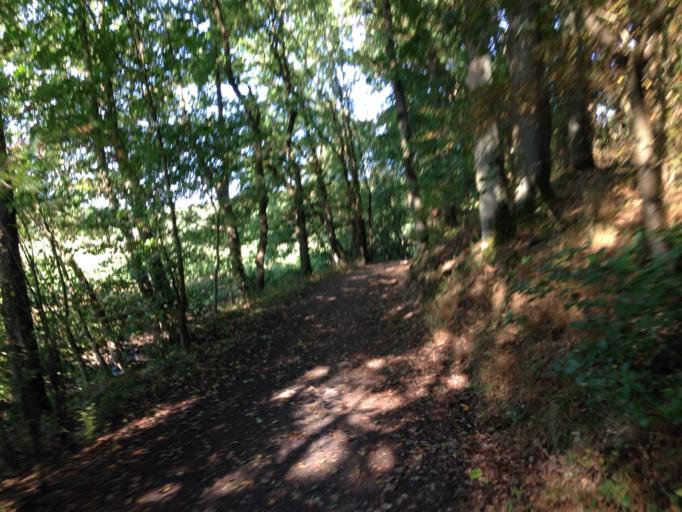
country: DE
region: Hesse
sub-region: Regierungsbezirk Giessen
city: Heuchelheim
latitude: 50.6263
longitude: 8.6475
